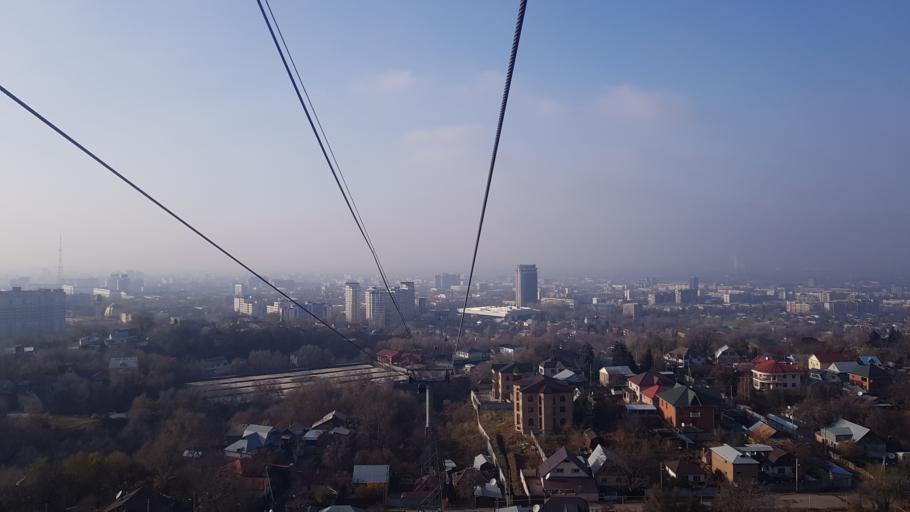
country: KZ
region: Almaty Qalasy
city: Almaty
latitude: 43.2364
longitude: 76.9713
